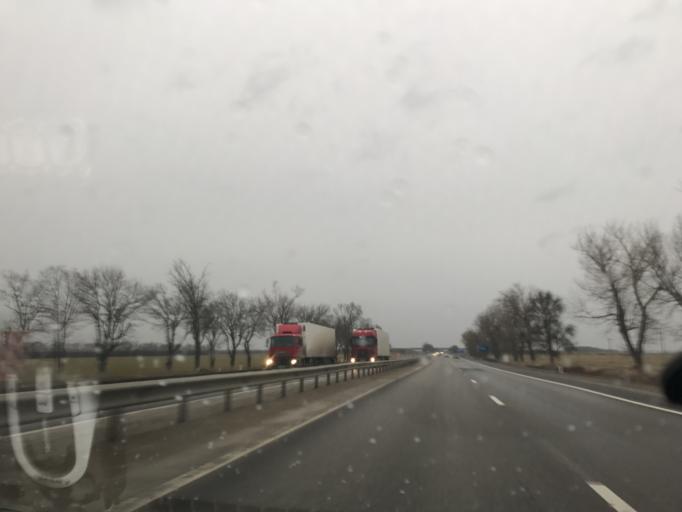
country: RU
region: Krasnodarskiy
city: Pavlovskaya
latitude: 46.1557
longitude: 39.8466
